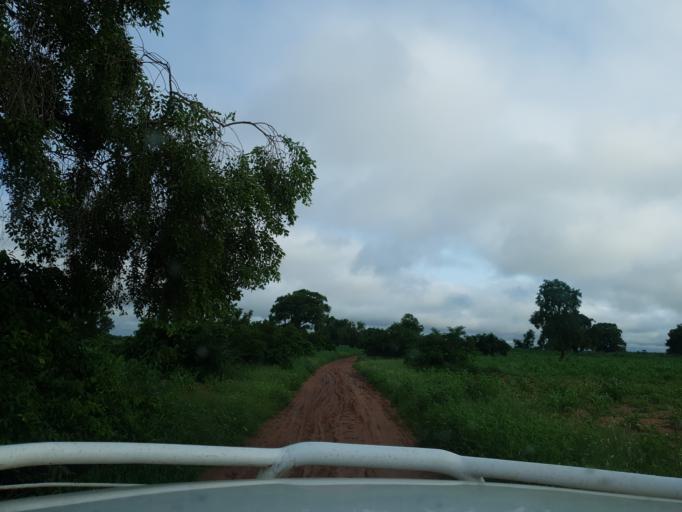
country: ML
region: Segou
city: Baroueli
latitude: 13.4000
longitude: -7.0063
